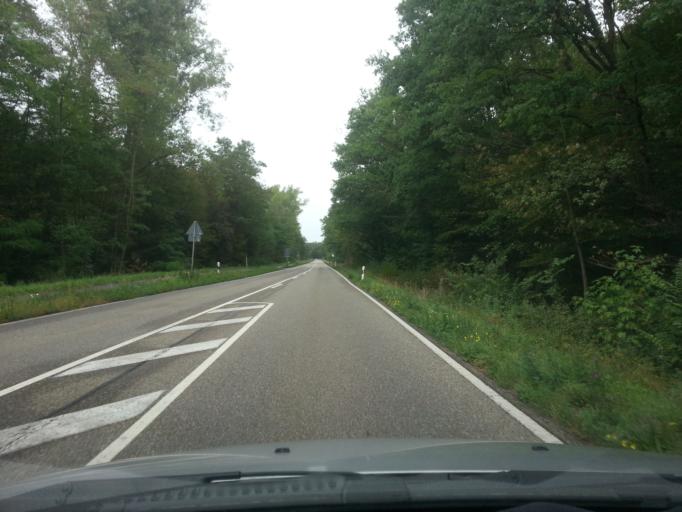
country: DE
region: Rheinland-Pfalz
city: Offenbach an der Queich
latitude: 49.2045
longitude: 8.1899
